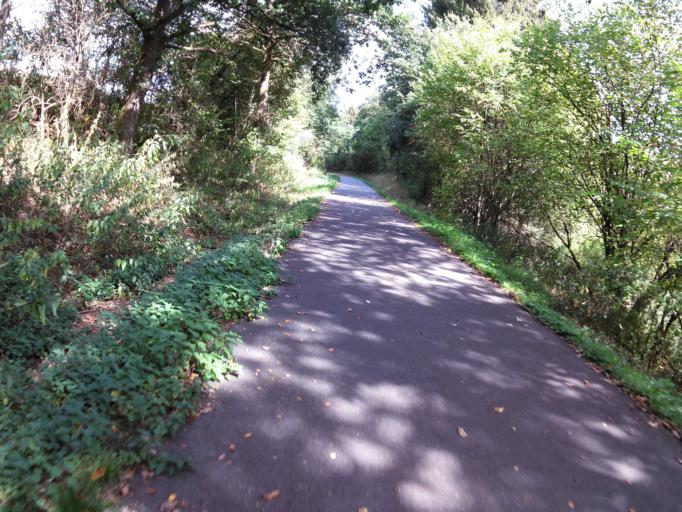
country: DE
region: Rheinland-Pfalz
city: Kickeshausen
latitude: 50.0630
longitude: 6.2466
